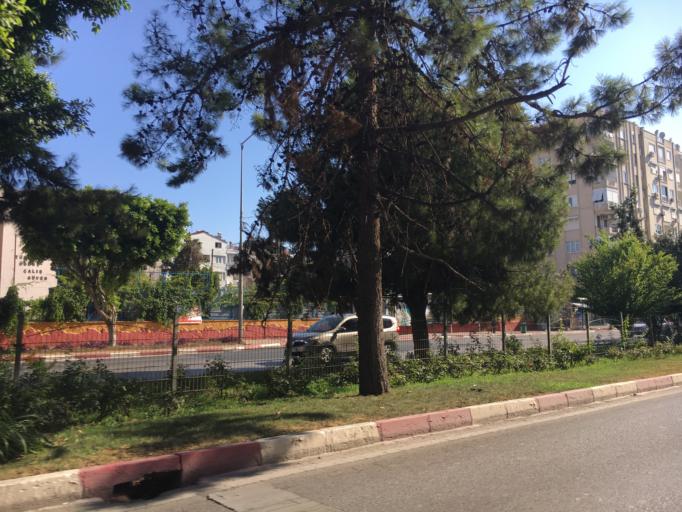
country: TR
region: Antalya
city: Antalya
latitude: 36.8891
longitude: 30.6843
